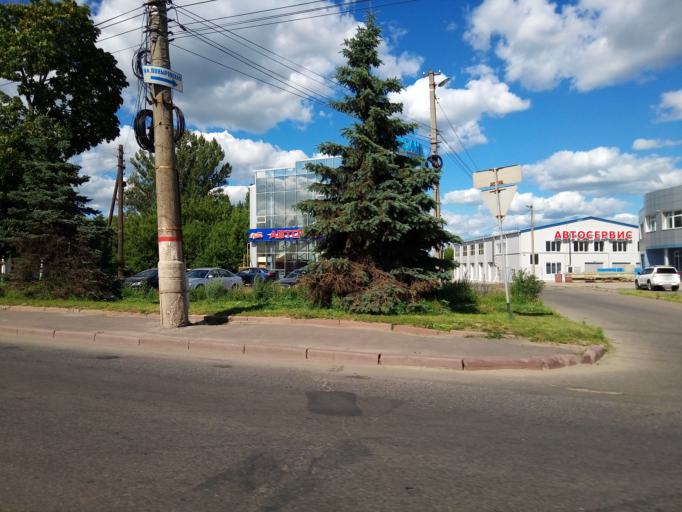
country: RU
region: Kursk
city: Kursk
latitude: 51.7846
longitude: 36.1728
